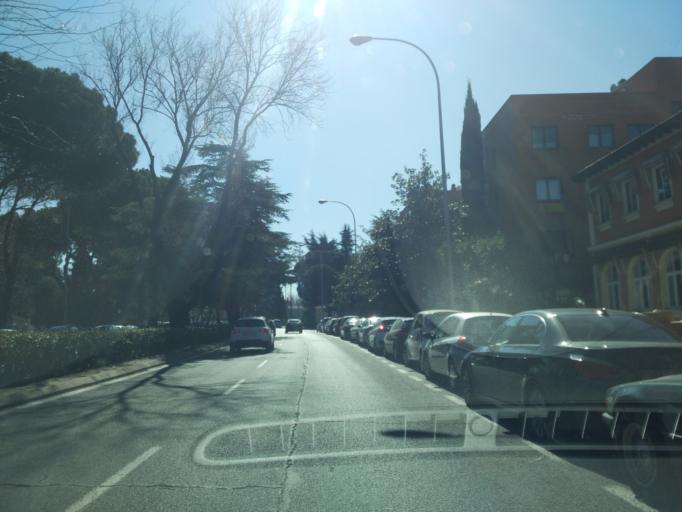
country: ES
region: Madrid
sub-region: Provincia de Madrid
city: Chamartin
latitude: 40.4640
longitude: -3.6653
